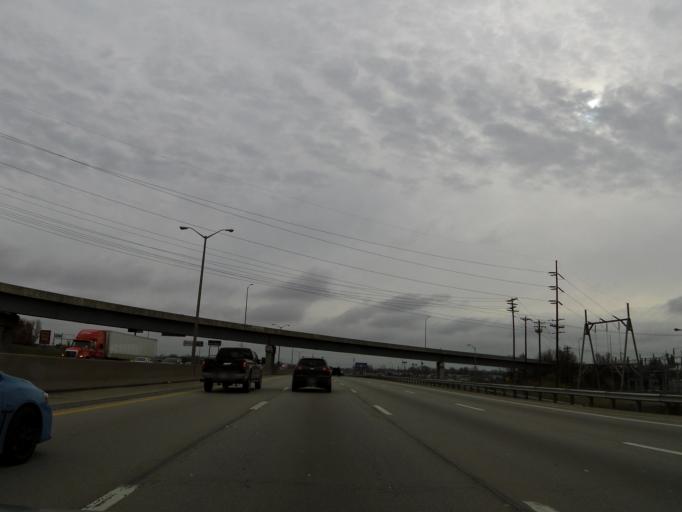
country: US
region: Kentucky
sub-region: Boone County
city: Florence
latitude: 38.9920
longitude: -84.6447
